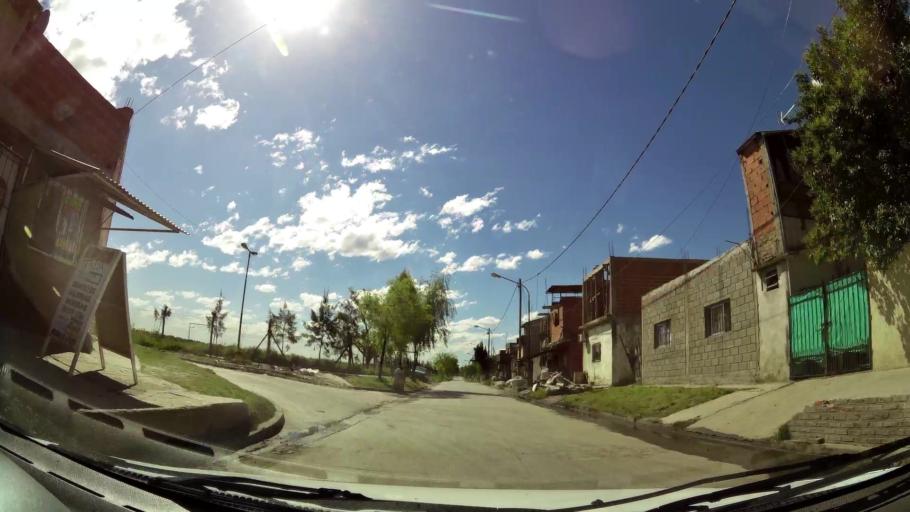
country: AR
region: Buenos Aires
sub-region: Partido de General San Martin
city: General San Martin
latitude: -34.5141
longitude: -58.5844
